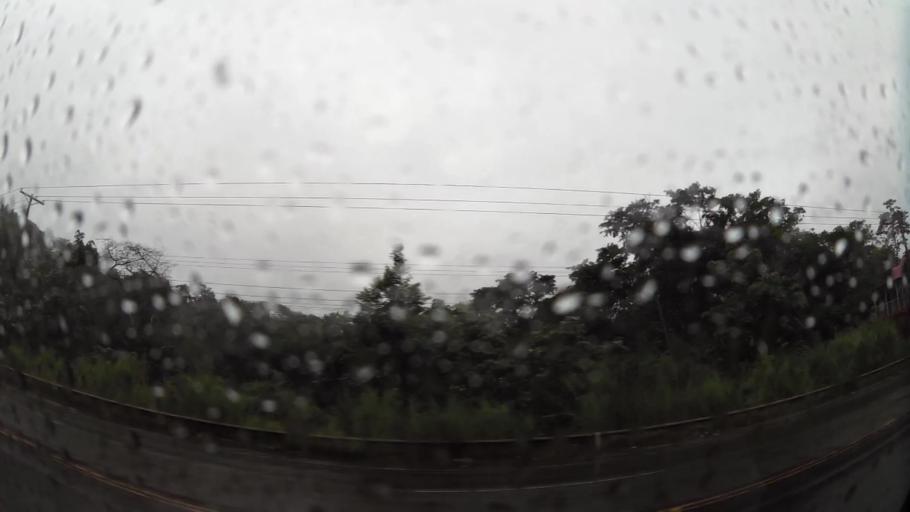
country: PA
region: Colon
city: Santa Rita Arriba
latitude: 9.3304
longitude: -79.8021
